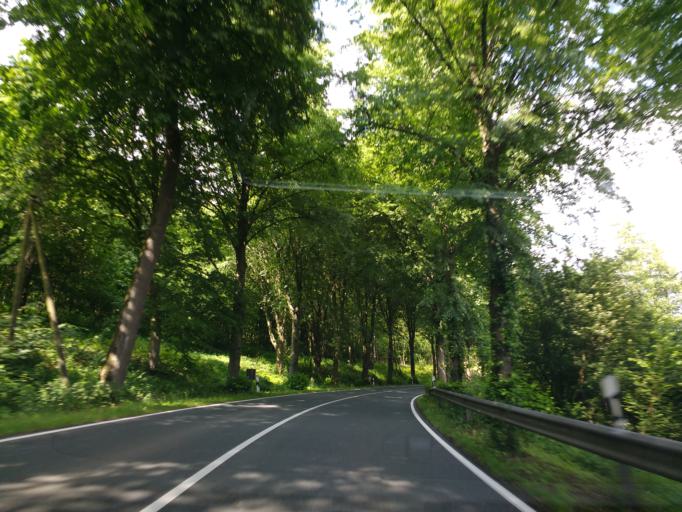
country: DE
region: North Rhine-Westphalia
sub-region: Regierungsbezirk Detmold
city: Lemgo
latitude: 52.0711
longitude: 8.9179
